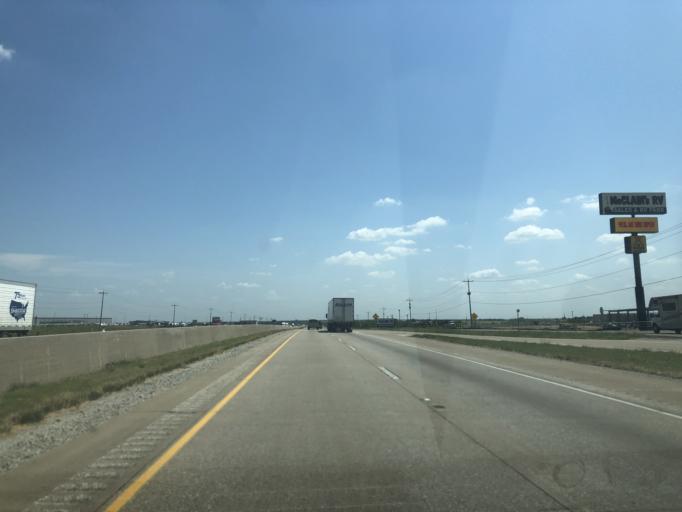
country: US
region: Texas
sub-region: Denton County
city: Sanger
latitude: 33.4032
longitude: -97.1766
